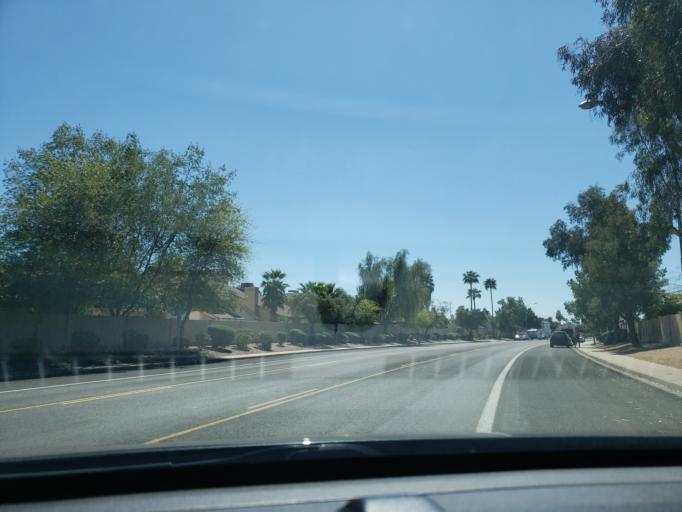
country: US
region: Arizona
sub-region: Maricopa County
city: Gilbert
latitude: 33.3837
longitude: -111.7474
